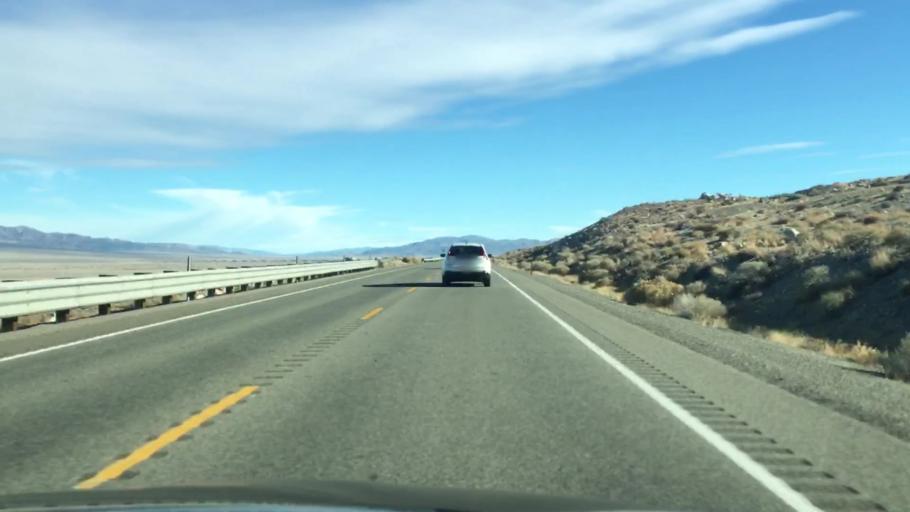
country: US
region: Nevada
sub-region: Mineral County
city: Hawthorne
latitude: 38.6144
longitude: -118.7251
